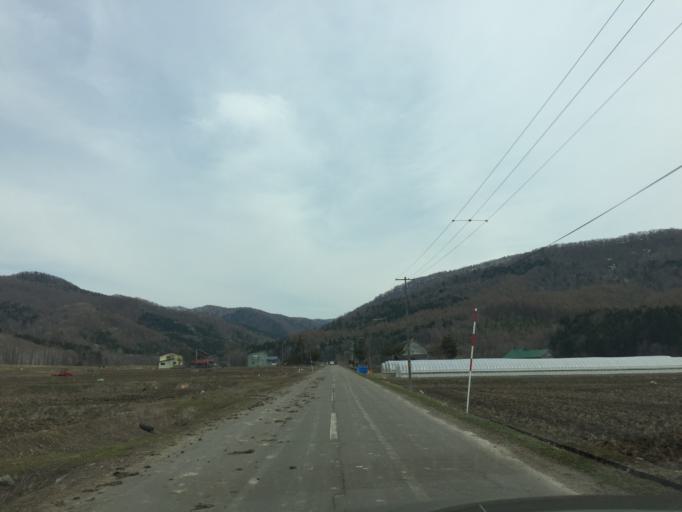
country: JP
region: Hokkaido
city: Ashibetsu
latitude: 43.6197
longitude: 142.2167
